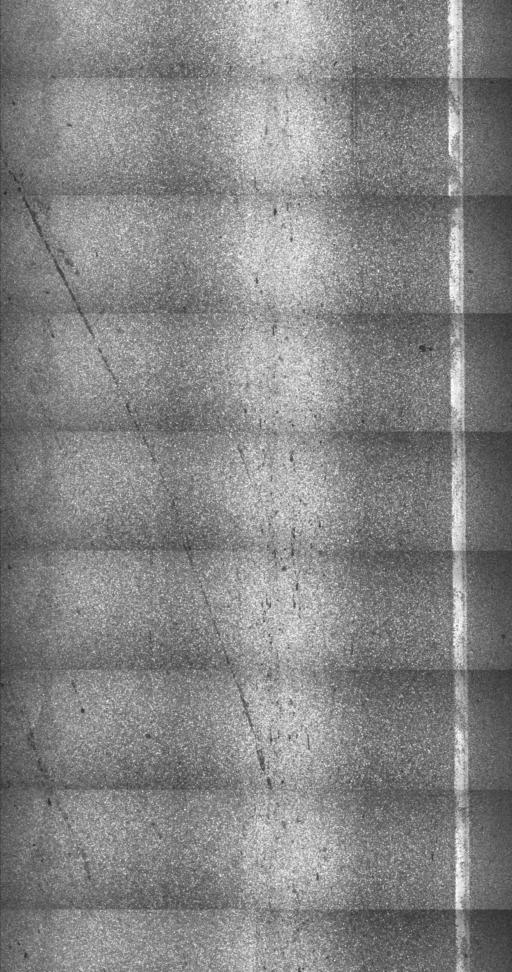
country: US
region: Vermont
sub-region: Franklin County
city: Enosburg Falls
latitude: 44.9073
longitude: -72.8183
